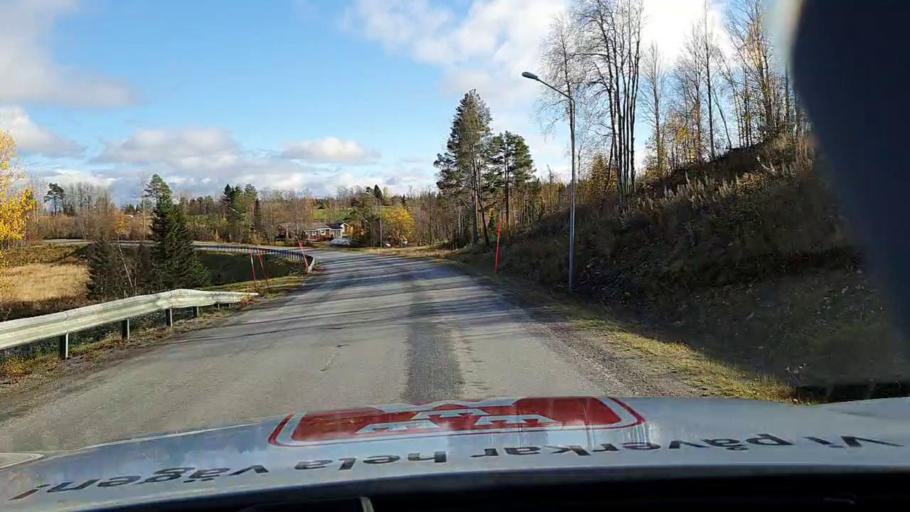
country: SE
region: Jaemtland
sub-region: Krokoms Kommun
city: Krokom
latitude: 63.1833
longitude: 14.0422
